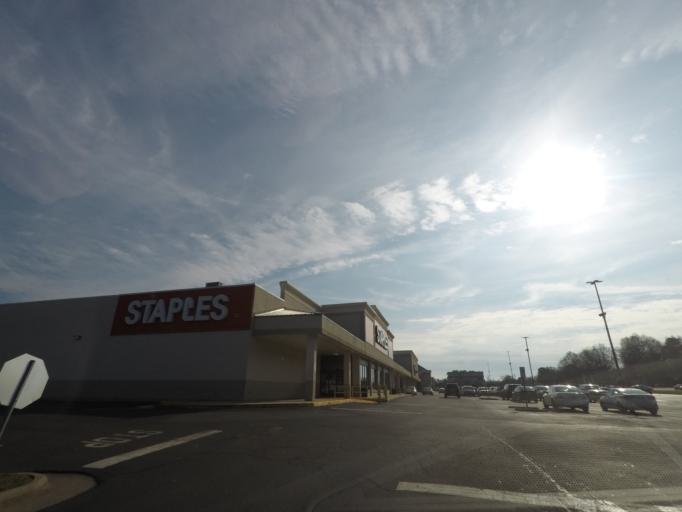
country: US
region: North Carolina
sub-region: Durham County
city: Durham
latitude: 36.0505
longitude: -78.9051
